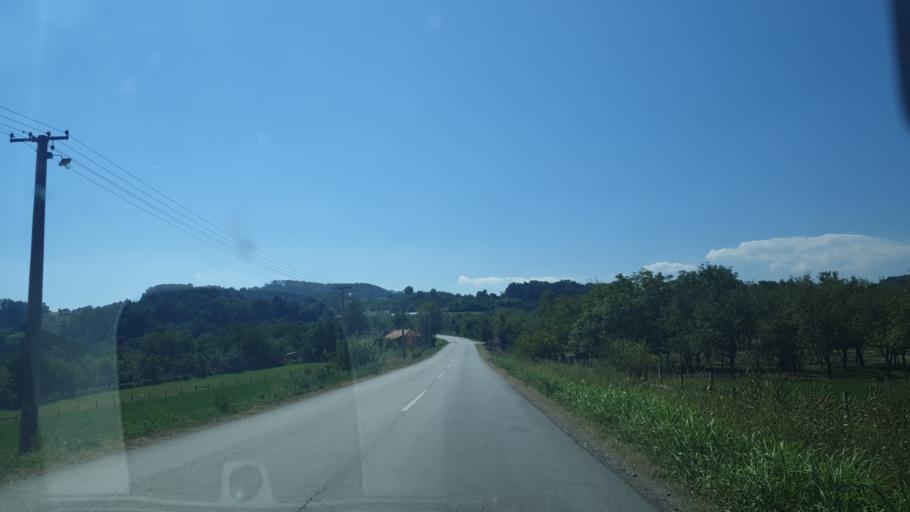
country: RS
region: Central Serbia
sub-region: Kolubarski Okrug
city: Mionica
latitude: 44.2303
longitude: 20.0837
